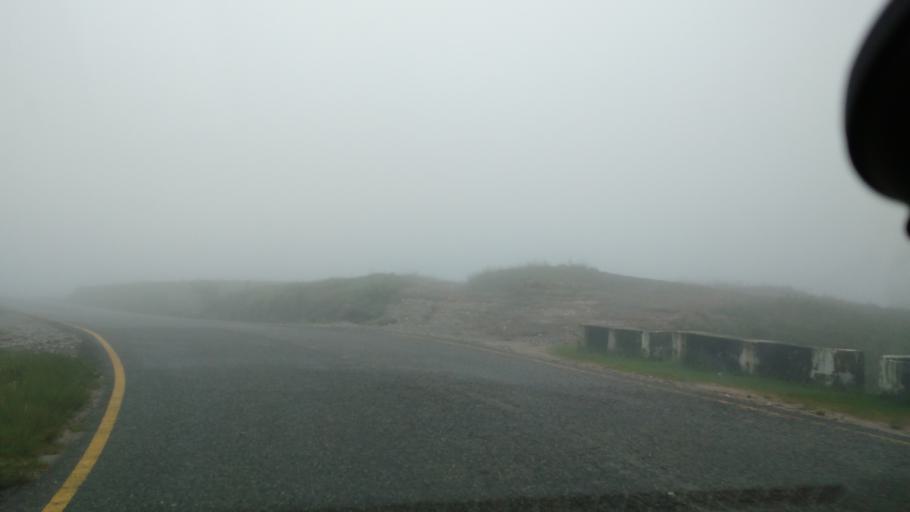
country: IN
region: Meghalaya
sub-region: East Khasi Hills
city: Cherrapunji
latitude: 25.3106
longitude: 91.7283
